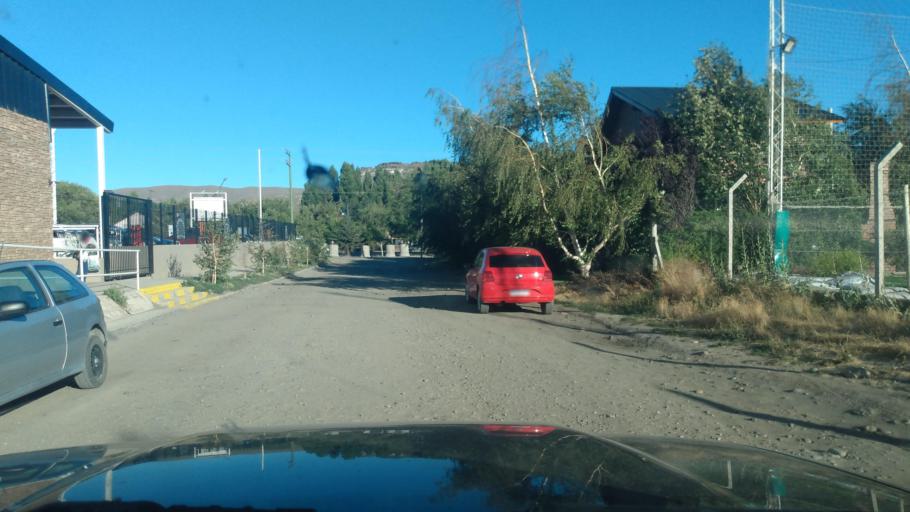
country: AR
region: Neuquen
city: Junin de los Andes
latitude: -39.9554
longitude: -71.0788
